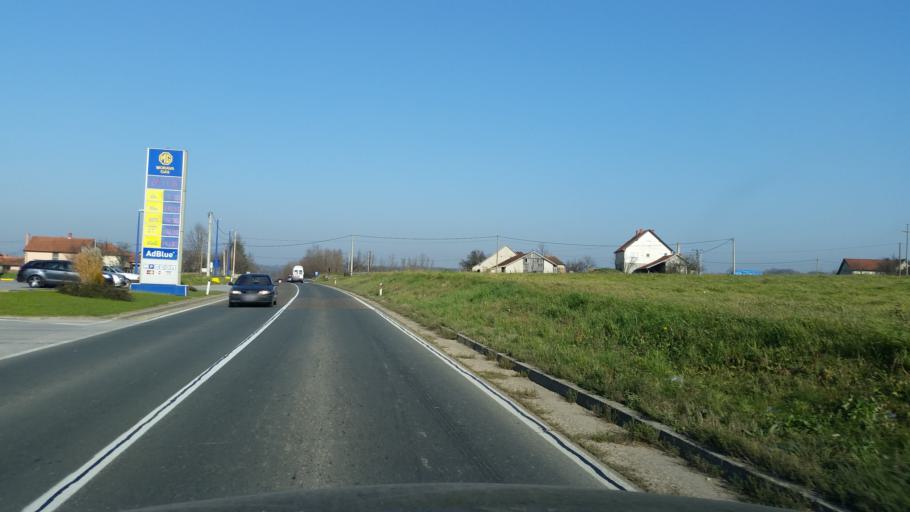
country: RS
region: Central Serbia
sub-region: Kolubarski Okrug
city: Ljig
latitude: 44.2490
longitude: 20.2842
